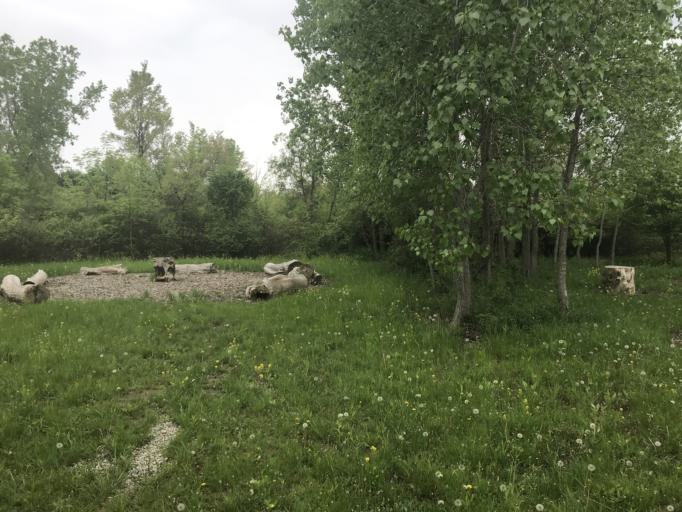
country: US
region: Michigan
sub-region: Eaton County
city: Dimondale
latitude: 42.6891
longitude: -84.6338
